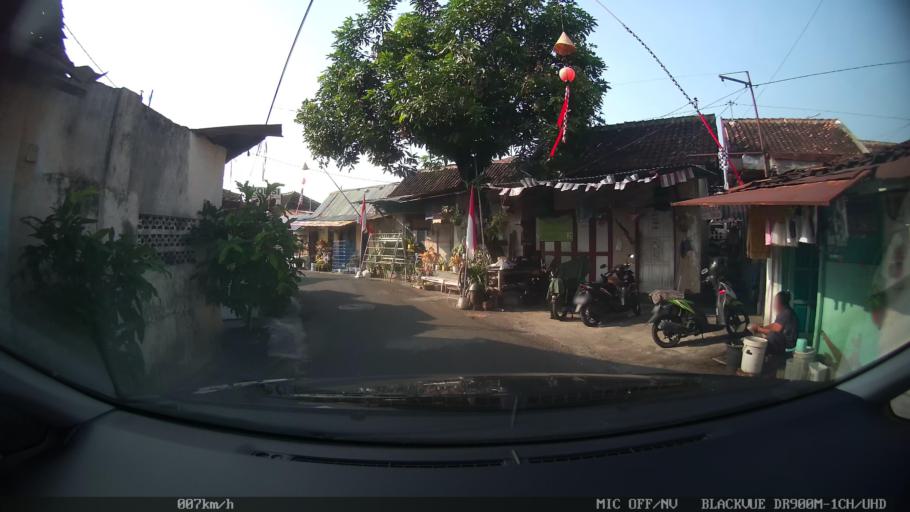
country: ID
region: Daerah Istimewa Yogyakarta
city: Yogyakarta
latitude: -7.8093
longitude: 110.3648
